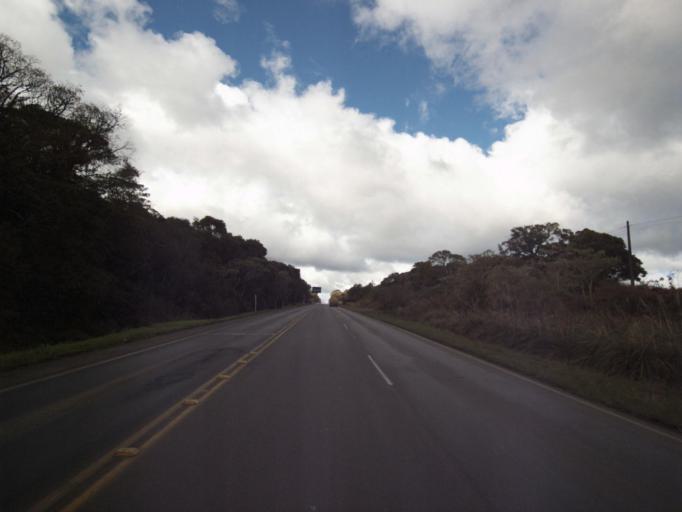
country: BR
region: Santa Catarina
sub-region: Concordia
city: Concordia
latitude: -26.9707
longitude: -51.8517
